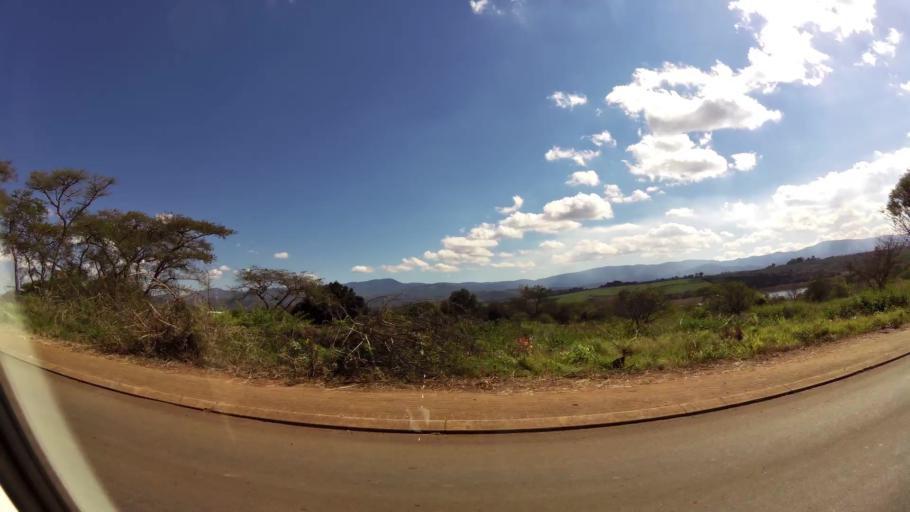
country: ZA
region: Limpopo
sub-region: Mopani District Municipality
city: Tzaneen
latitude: -23.8191
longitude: 30.1445
